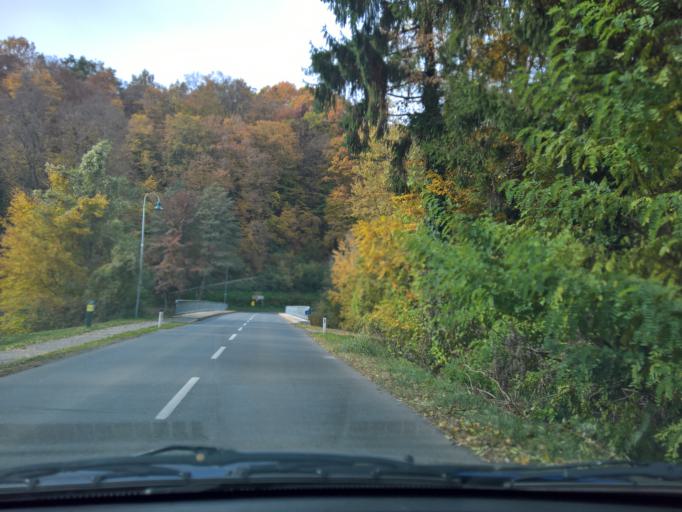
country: AT
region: Styria
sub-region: Politischer Bezirk Leibnitz
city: Leibnitz
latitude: 46.7804
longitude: 15.5268
